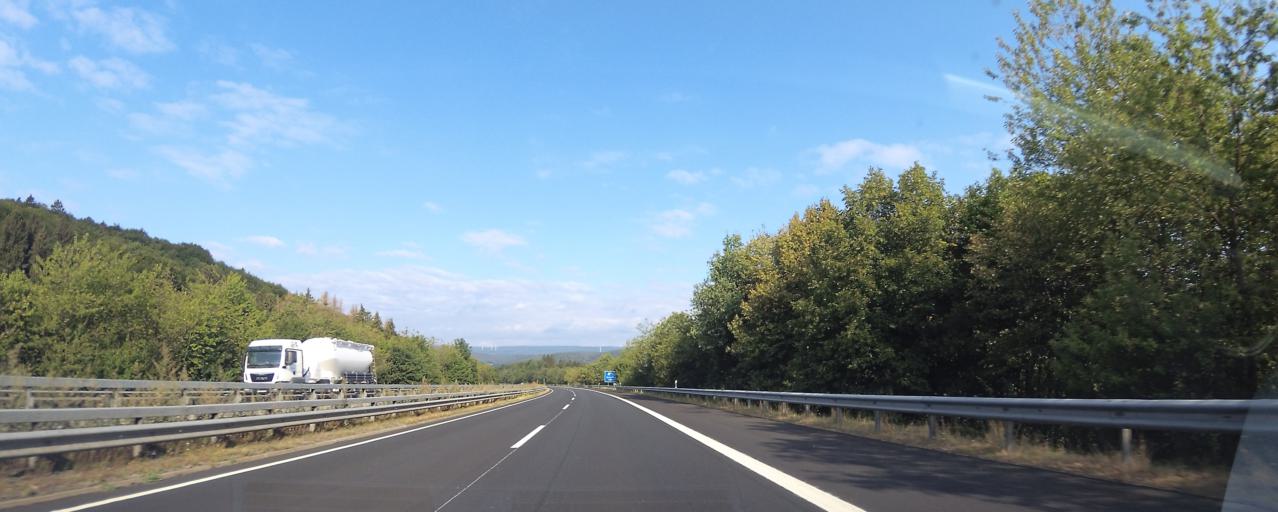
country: DE
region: Rheinland-Pfalz
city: Gimbweiler
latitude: 49.5999
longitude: 7.1872
